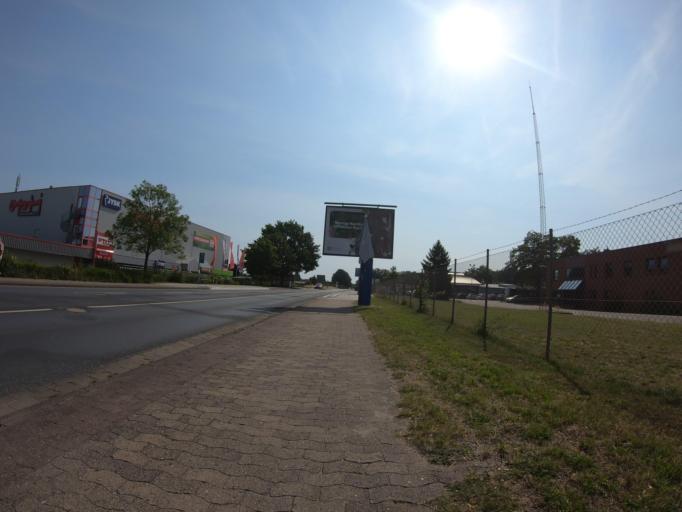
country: DE
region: Lower Saxony
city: Gifhorn
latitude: 52.4633
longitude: 10.5433
